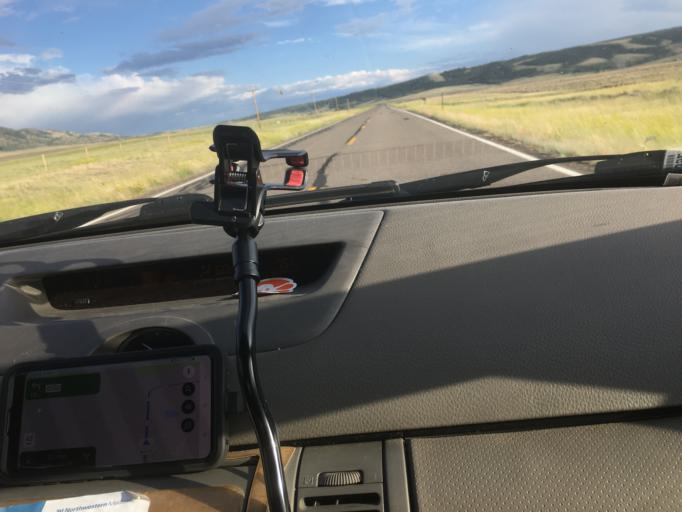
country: US
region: Wyoming
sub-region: Albany County
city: Laramie
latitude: 41.2155
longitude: -106.0892
